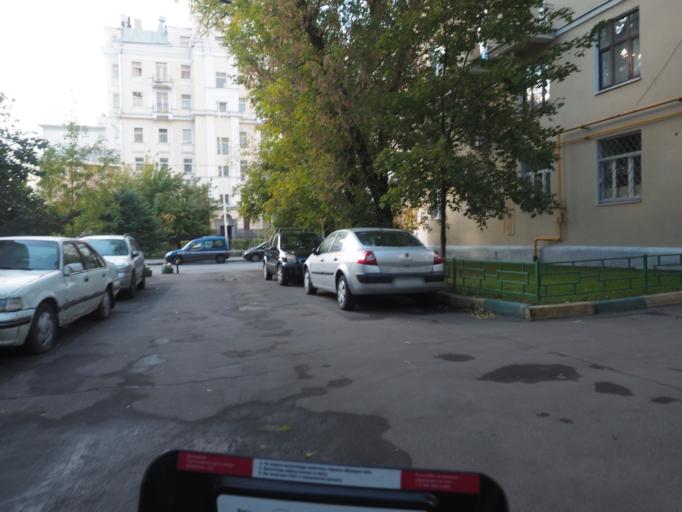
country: RU
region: Moscow
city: Moscow
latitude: 55.7691
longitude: 37.6367
